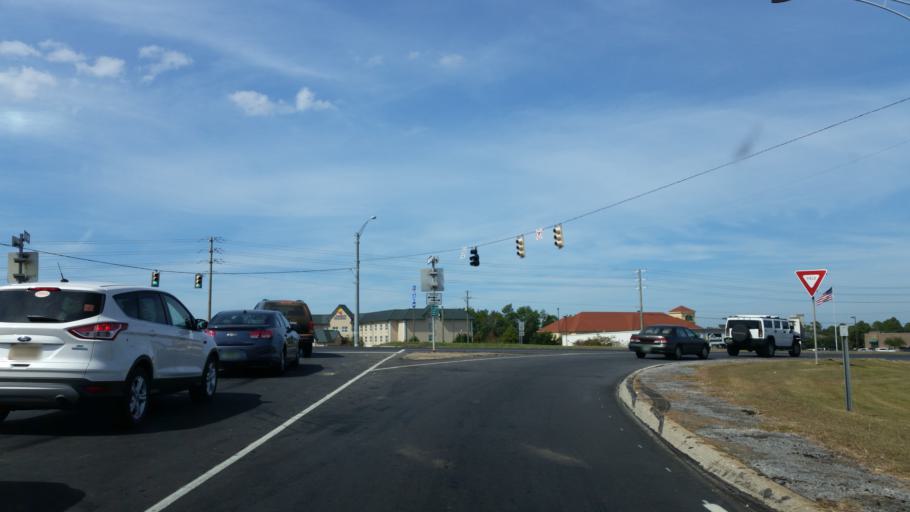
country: US
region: Alabama
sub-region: Baldwin County
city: Spanish Fort
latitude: 30.6643
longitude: -87.8516
